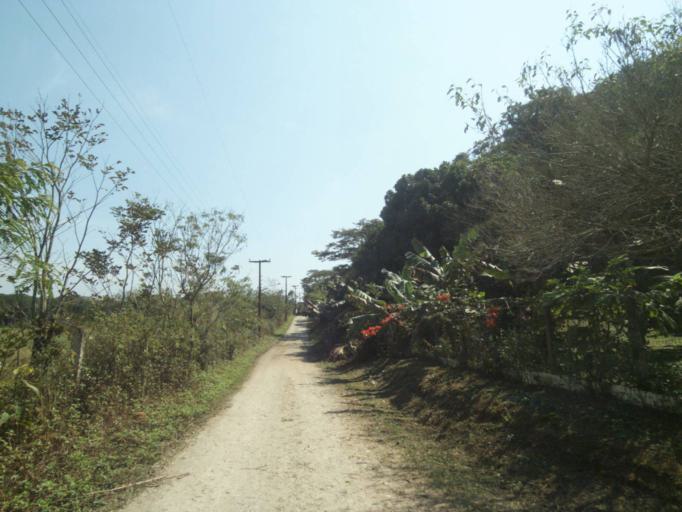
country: BR
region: Parana
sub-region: Paranagua
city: Paranagua
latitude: -25.5483
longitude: -48.5915
